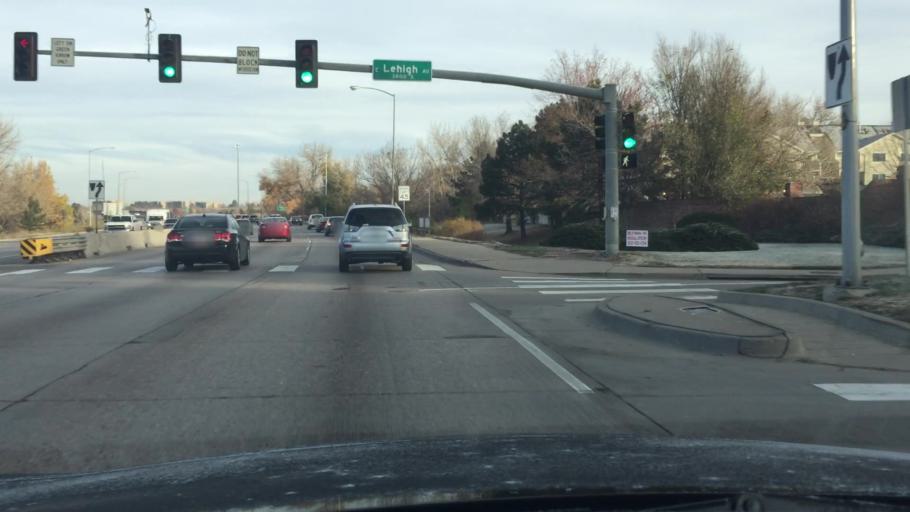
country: US
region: Colorado
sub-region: Arapahoe County
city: Dove Valley
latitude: 39.6473
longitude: -104.8287
